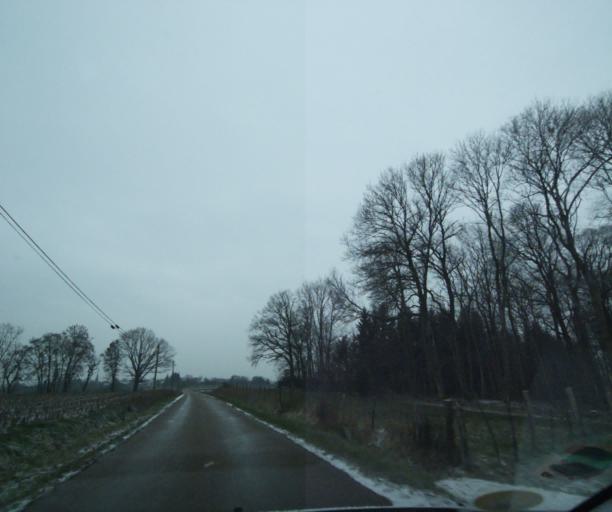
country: FR
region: Champagne-Ardenne
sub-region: Departement de la Haute-Marne
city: Wassy
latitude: 48.4658
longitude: 5.0349
